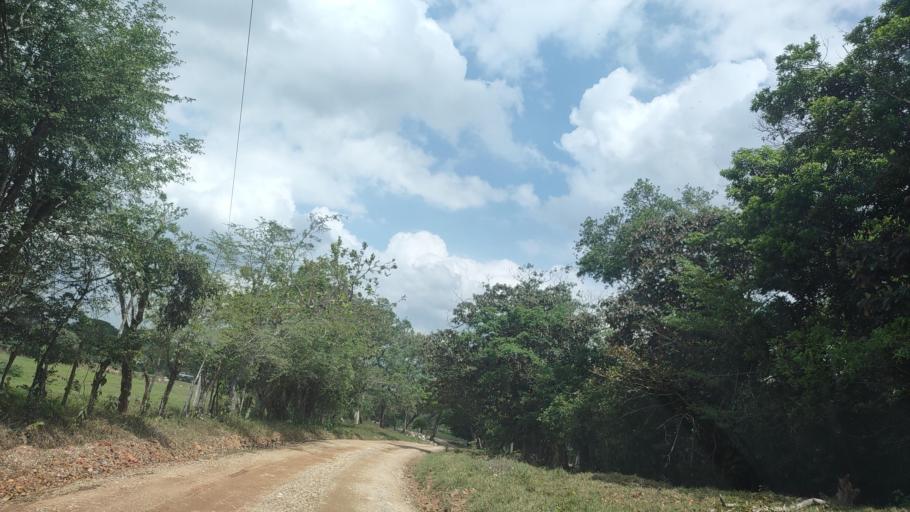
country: MX
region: Veracruz
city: Las Choapas
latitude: 17.9589
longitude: -94.1172
